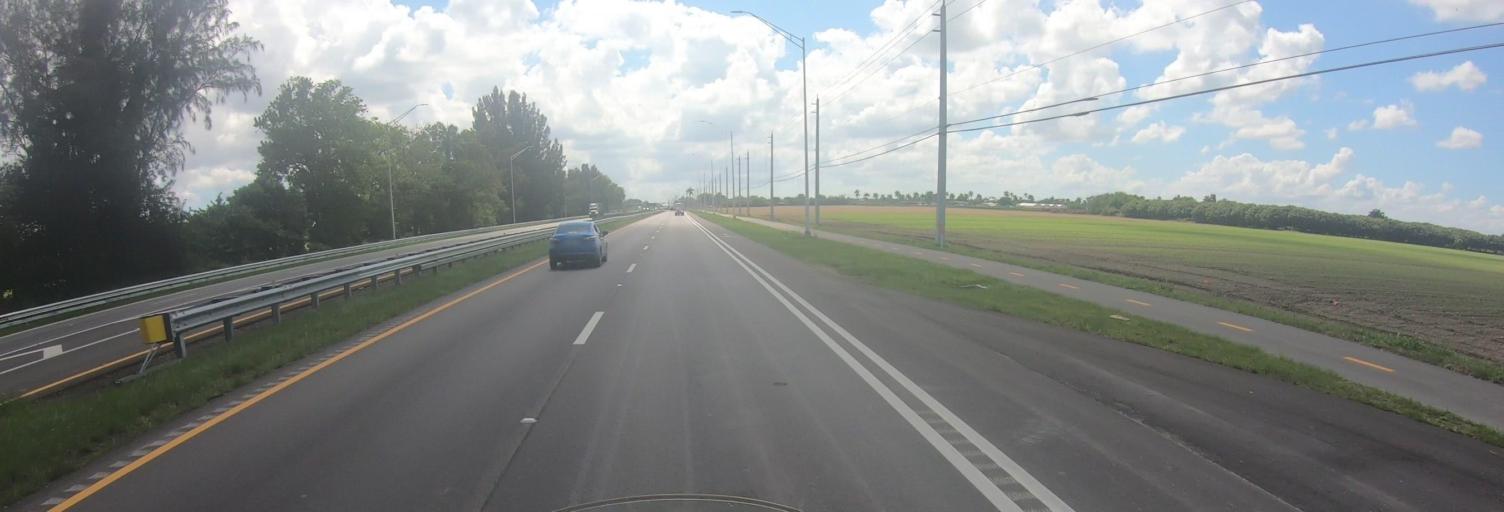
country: US
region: Florida
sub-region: Miami-Dade County
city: Naranja
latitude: 25.5428
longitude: -80.4787
